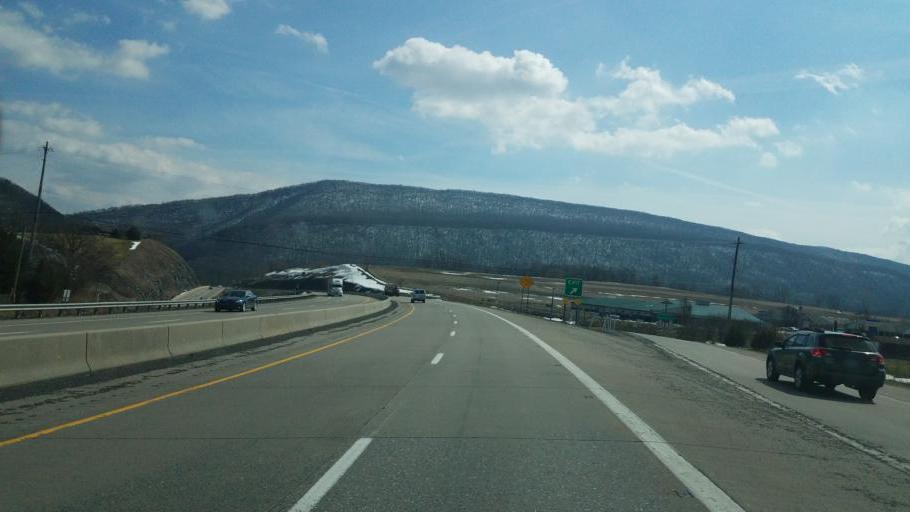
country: US
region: Pennsylvania
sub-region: Mifflin County
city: Church Hill
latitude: 40.6699
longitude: -77.6046
